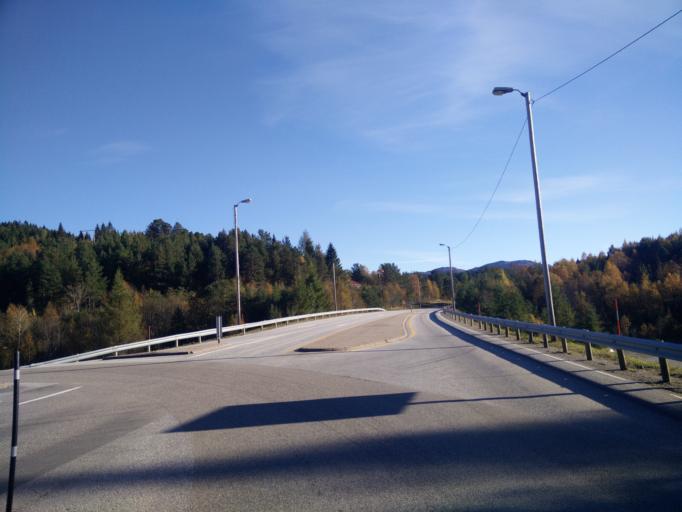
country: NO
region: More og Romsdal
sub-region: Kristiansund
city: Rensvik
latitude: 63.0116
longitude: 8.0004
